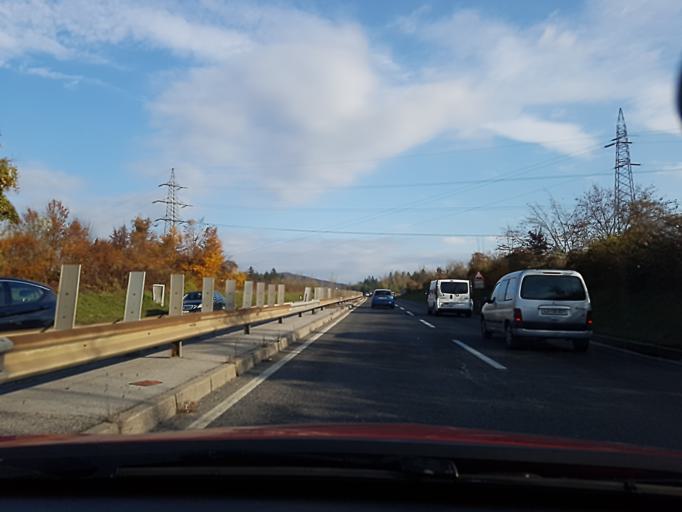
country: SI
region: Ljubljana
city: Ljubljana
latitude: 46.0853
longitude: 14.5310
